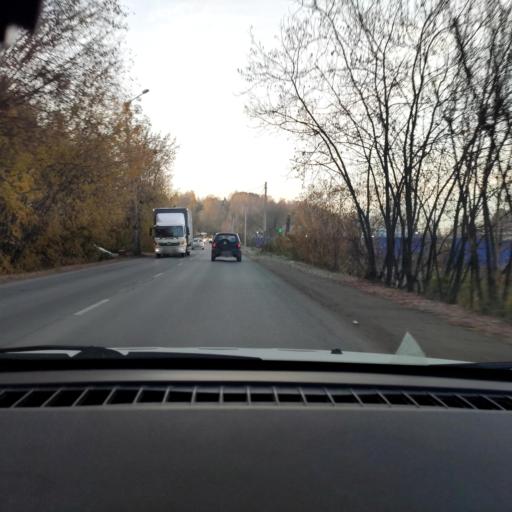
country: RU
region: Perm
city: Perm
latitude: 58.0600
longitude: 56.3382
